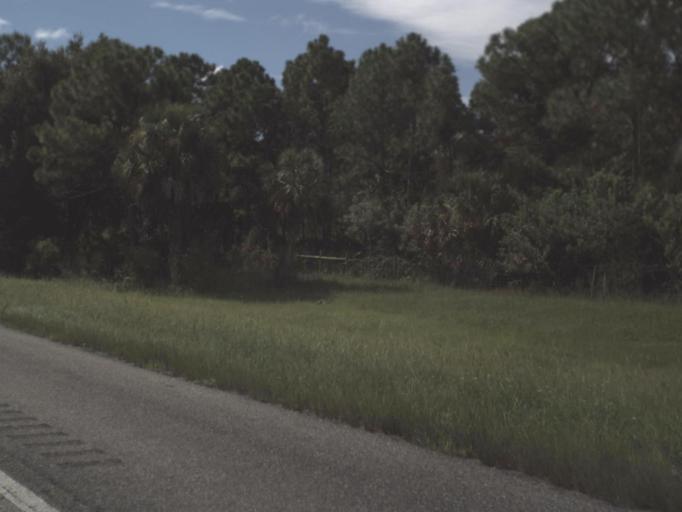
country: US
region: Florida
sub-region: Charlotte County
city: Port Charlotte
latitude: 27.0381
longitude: -82.0610
